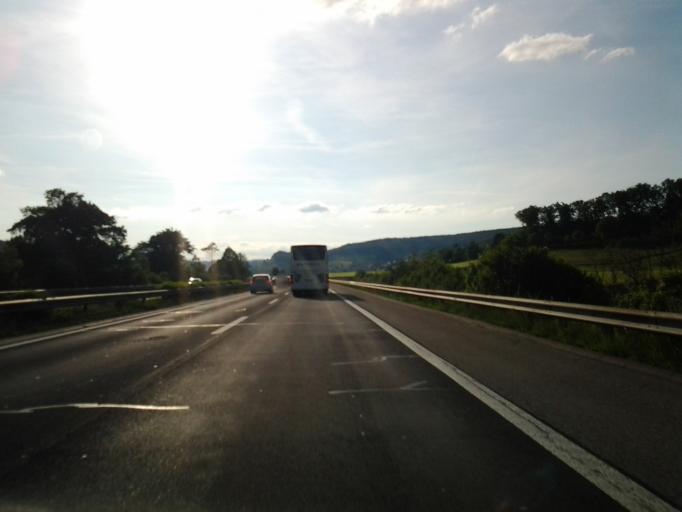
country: CH
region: Lucerne
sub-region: Sursee District
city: Knutwil
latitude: 47.2018
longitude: 8.0527
